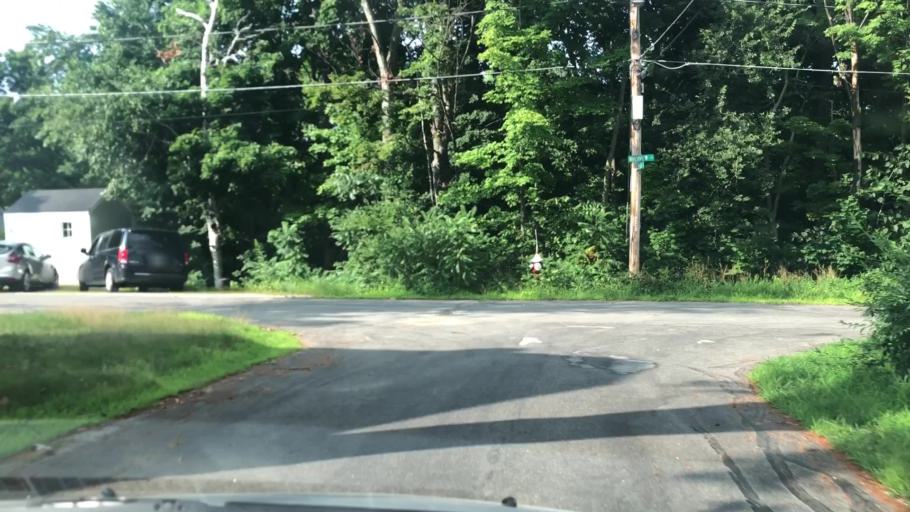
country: US
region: New Hampshire
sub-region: Hillsborough County
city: Milford
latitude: 42.8317
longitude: -71.6368
